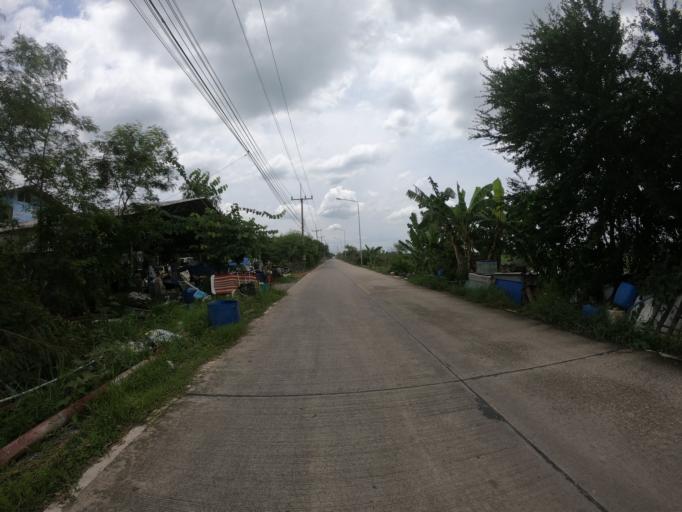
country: TH
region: Pathum Thani
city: Ban Lam Luk Ka
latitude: 13.9584
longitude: 100.8539
